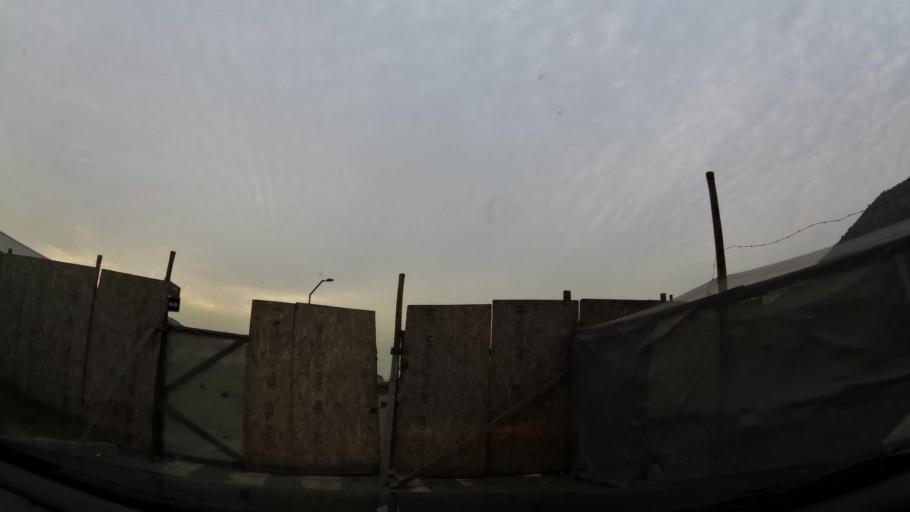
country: CL
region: Santiago Metropolitan
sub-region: Provincia de Chacabuco
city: Chicureo Abajo
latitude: -33.3156
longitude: -70.6512
